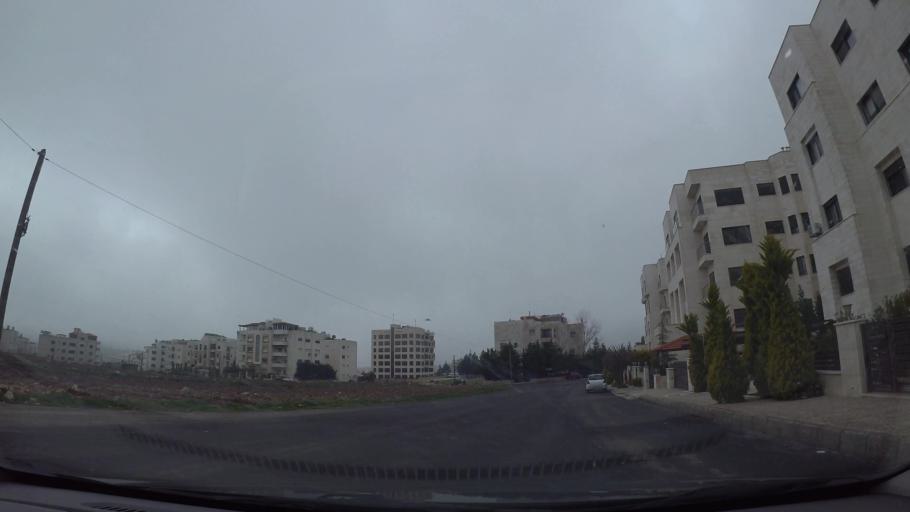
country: JO
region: Amman
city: Wadi as Sir
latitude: 31.9409
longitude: 35.8584
